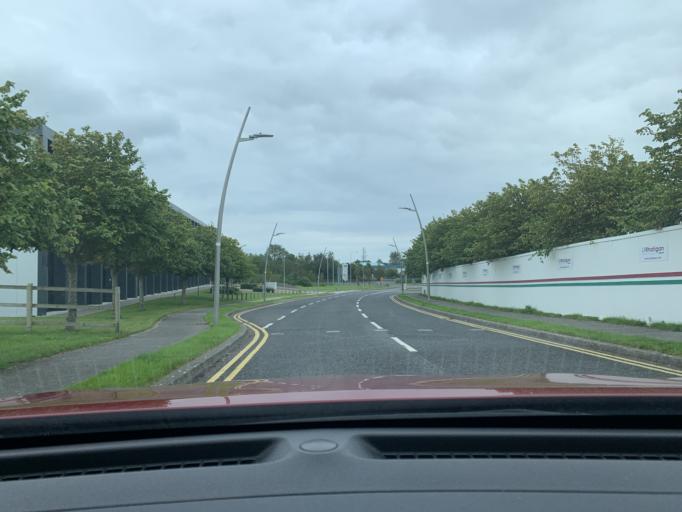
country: IE
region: Connaught
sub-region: Sligo
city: Sligo
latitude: 54.2777
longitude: -8.5046
